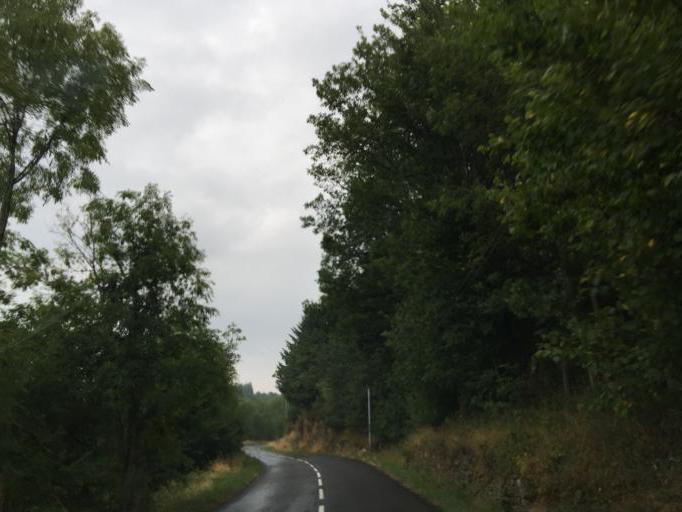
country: FR
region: Rhone-Alpes
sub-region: Departement de la Loire
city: Saint-Christo-en-Jarez
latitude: 45.5202
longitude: 4.4987
